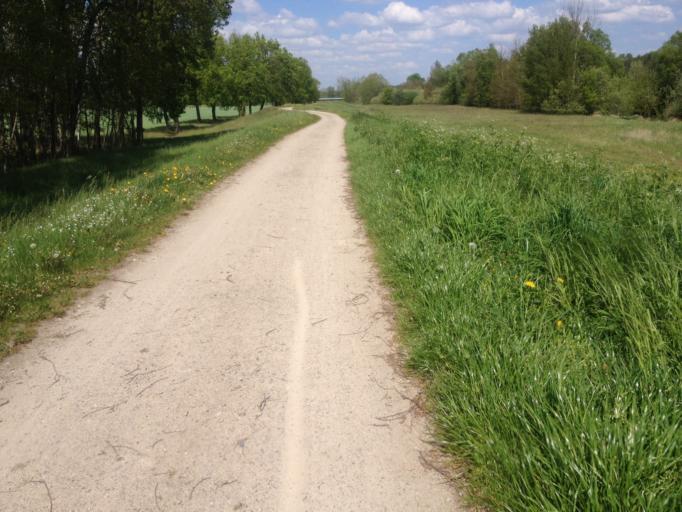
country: DE
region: Brandenburg
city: Drehnow
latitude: 51.8213
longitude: 14.3540
